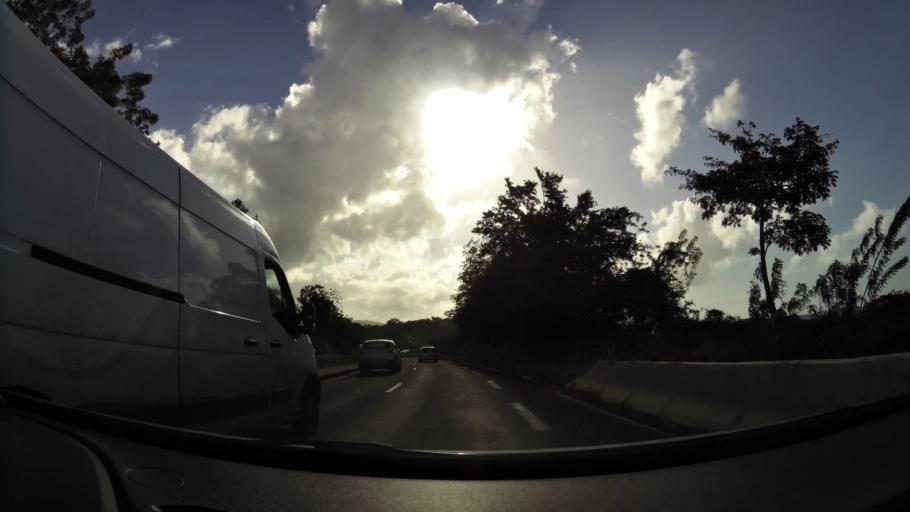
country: MQ
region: Martinique
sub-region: Martinique
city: Ducos
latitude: 14.5619
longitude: -60.9776
